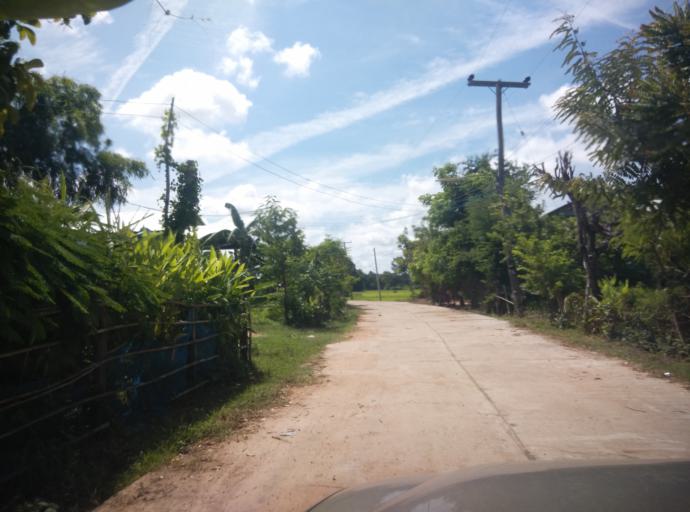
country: TH
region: Sisaket
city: Prang Ku
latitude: 14.9459
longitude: 104.0691
